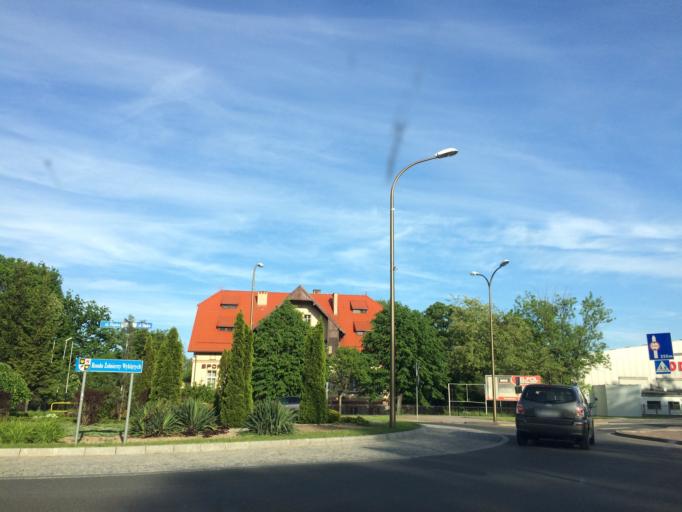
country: PL
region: Lower Silesian Voivodeship
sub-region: Powiat swidnicki
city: Swidnica
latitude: 50.8349
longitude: 16.4883
